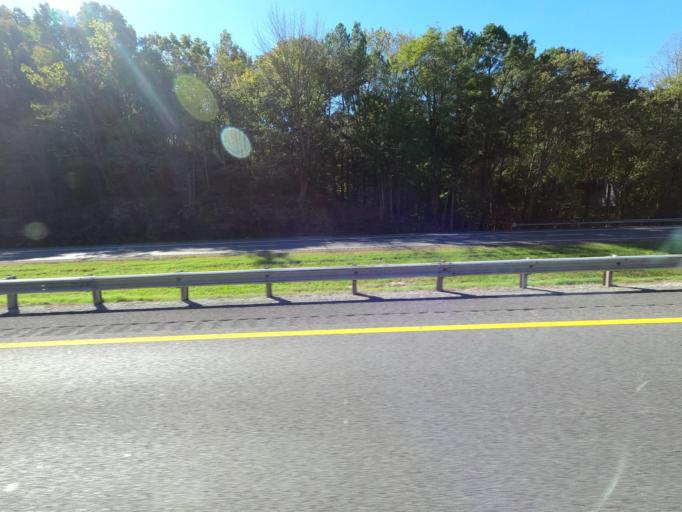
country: US
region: Tennessee
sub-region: Cheatham County
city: Pegram
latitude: 36.0774
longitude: -87.0315
